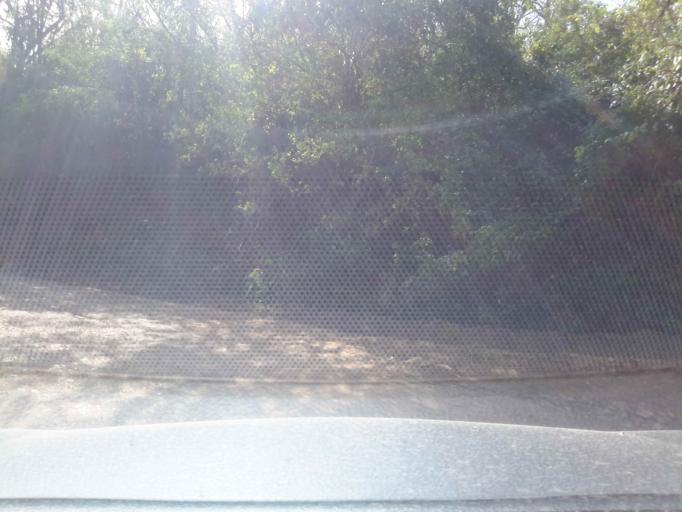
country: NI
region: Rivas
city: San Juan del Sur
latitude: 11.1851
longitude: -85.8008
